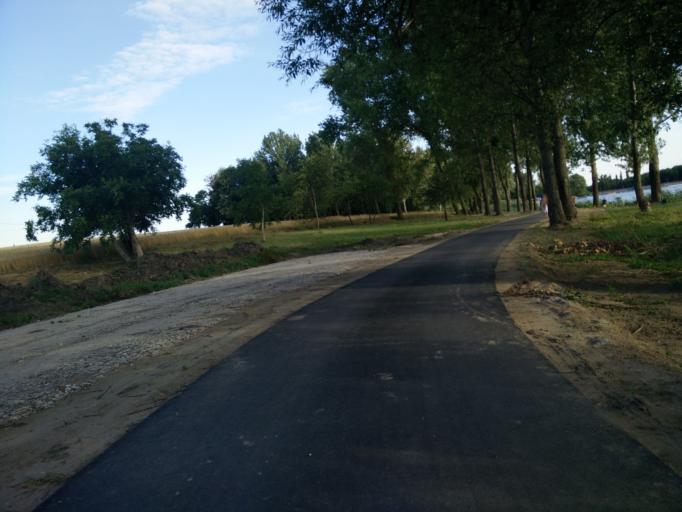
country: PL
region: Greater Poland Voivodeship
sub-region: Powiat sredzki
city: Sroda Wielkopolska
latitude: 52.2413
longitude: 17.2928
